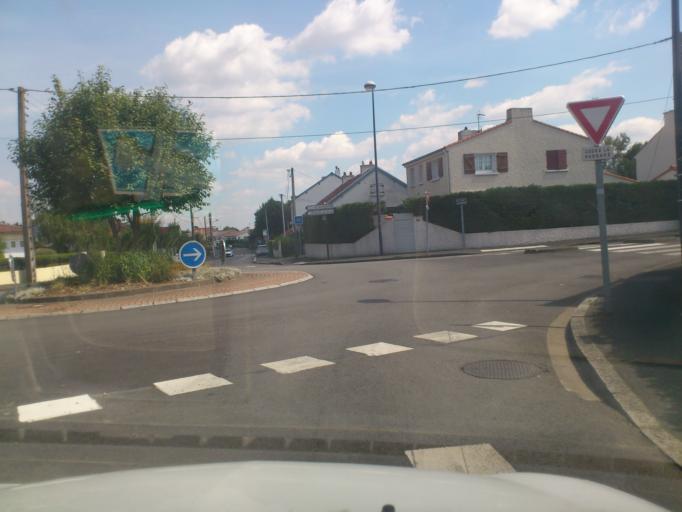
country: FR
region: Pays de la Loire
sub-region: Departement de la Loire-Atlantique
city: Reze
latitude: 47.1732
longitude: -1.5365
